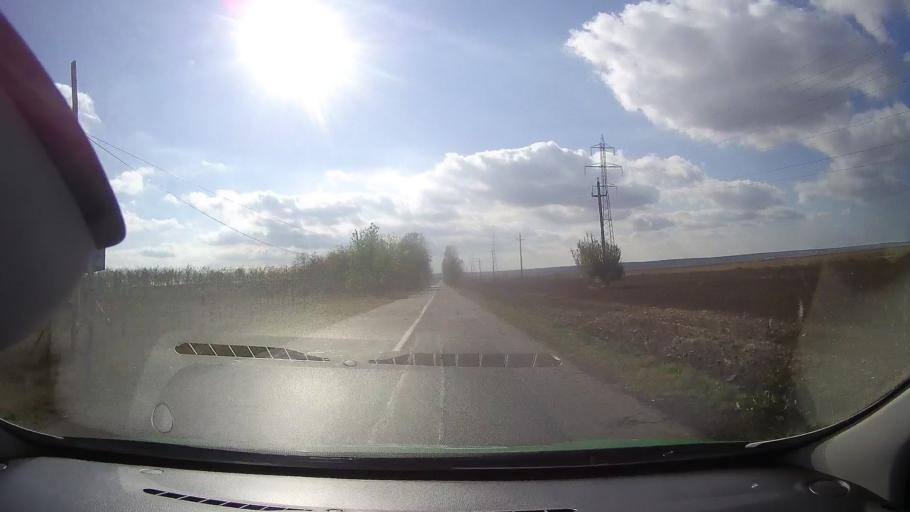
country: RO
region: Constanta
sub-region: Comuna Istria
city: Istria
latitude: 44.5456
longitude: 28.6923
